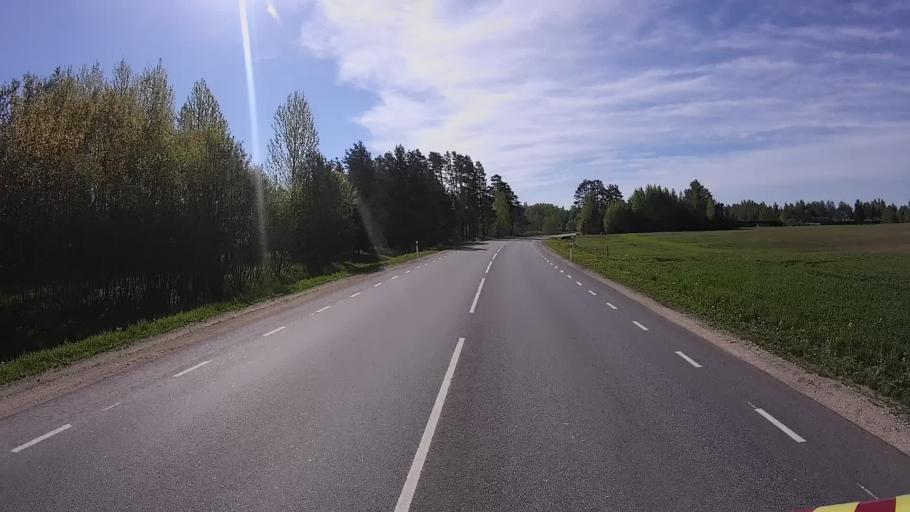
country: EE
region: Tartu
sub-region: UElenurme vald
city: Ulenurme
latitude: 58.3355
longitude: 26.9743
